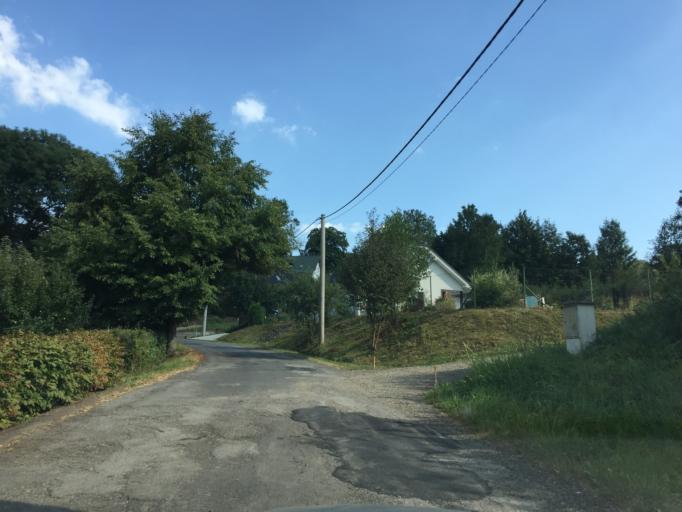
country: CZ
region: Liberecky
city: Mala Skala
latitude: 50.6709
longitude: 15.1718
